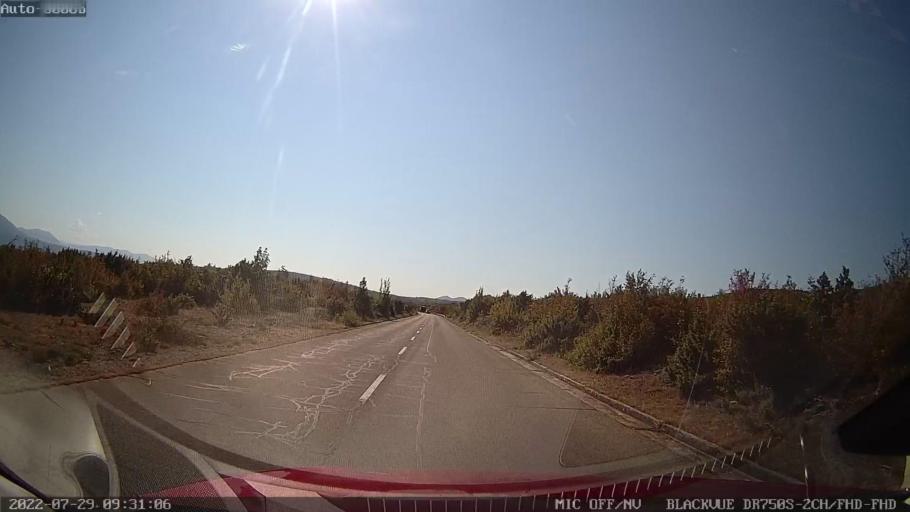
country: HR
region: Zadarska
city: Obrovac
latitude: 44.1910
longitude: 15.6947
